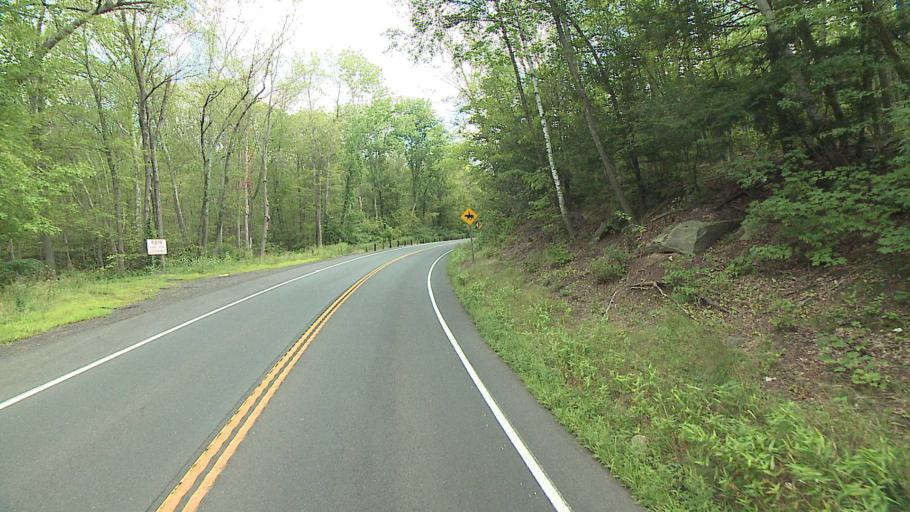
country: US
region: Connecticut
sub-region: Tolland County
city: Ellington
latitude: 41.9141
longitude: -72.4338
